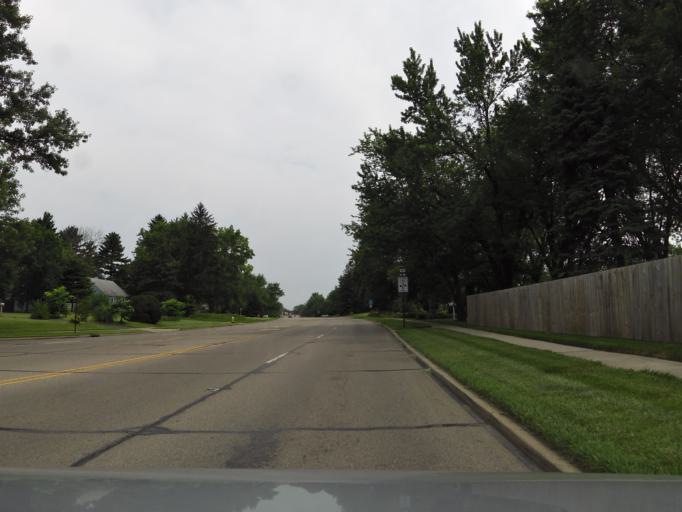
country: US
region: Ohio
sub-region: Montgomery County
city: Kettering
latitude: 39.6890
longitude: -84.1279
